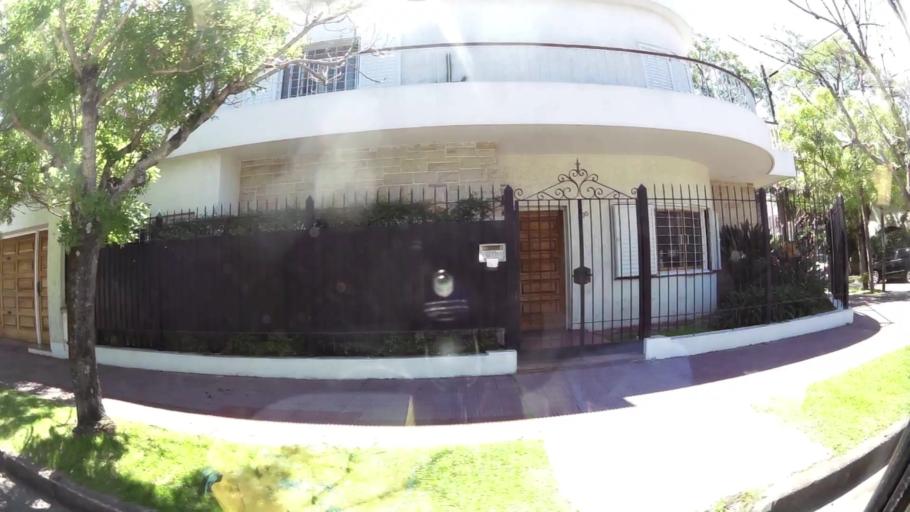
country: AR
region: Buenos Aires
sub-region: Partido de San Isidro
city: San Isidro
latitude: -34.4791
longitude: -58.5022
